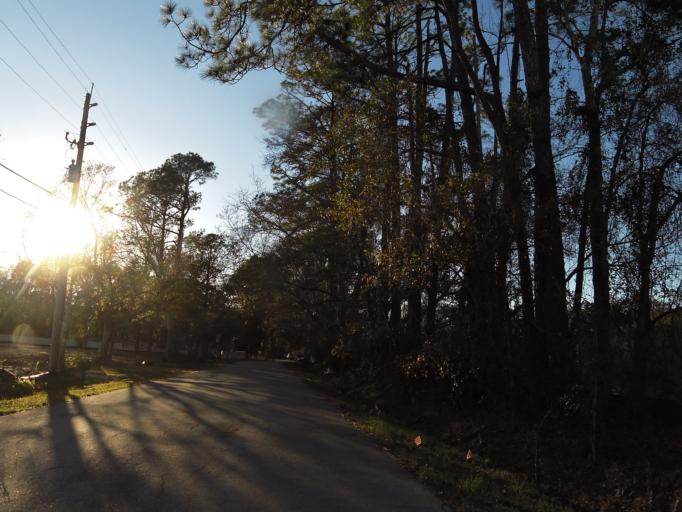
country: US
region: Florida
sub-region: Saint Johns County
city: Fruit Cove
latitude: 30.1988
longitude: -81.5820
